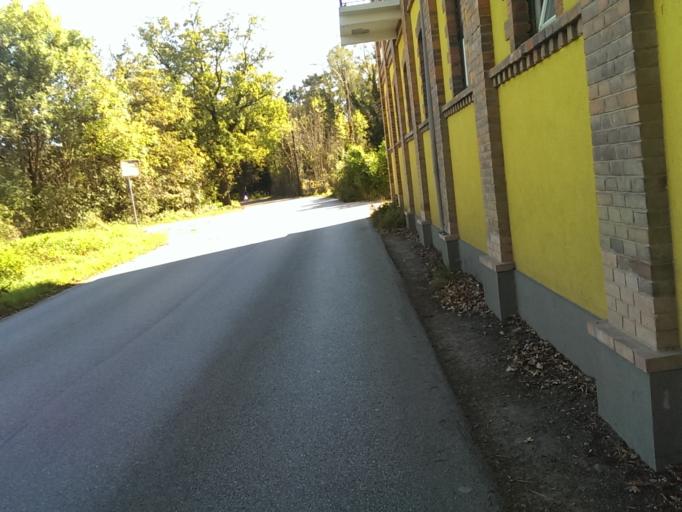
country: AT
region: Styria
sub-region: Politischer Bezirk Graz-Umgebung
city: Feldkirchen bei Graz
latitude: 47.0335
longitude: 15.4343
